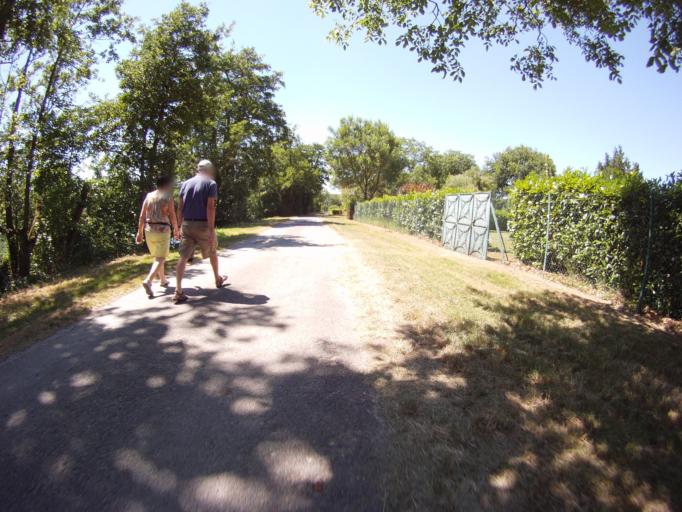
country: FR
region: Champagne-Ardenne
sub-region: Departement de la Marne
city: Damery
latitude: 49.0672
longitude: 3.8838
